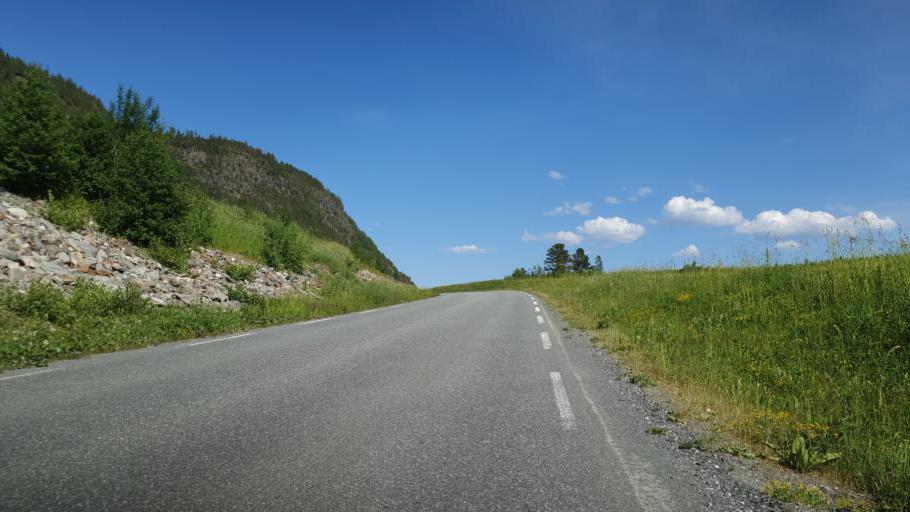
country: NO
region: Nord-Trondelag
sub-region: Leksvik
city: Leksvik
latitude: 63.6240
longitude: 10.5347
